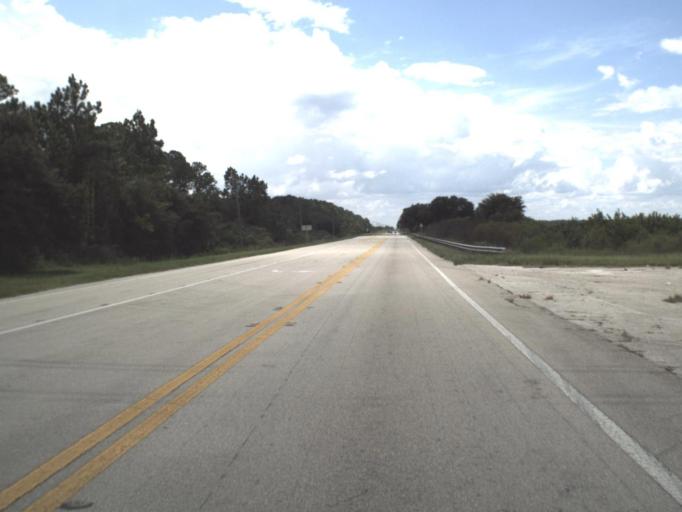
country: US
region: Florida
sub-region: Polk County
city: Babson Park
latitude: 27.8051
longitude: -81.2261
